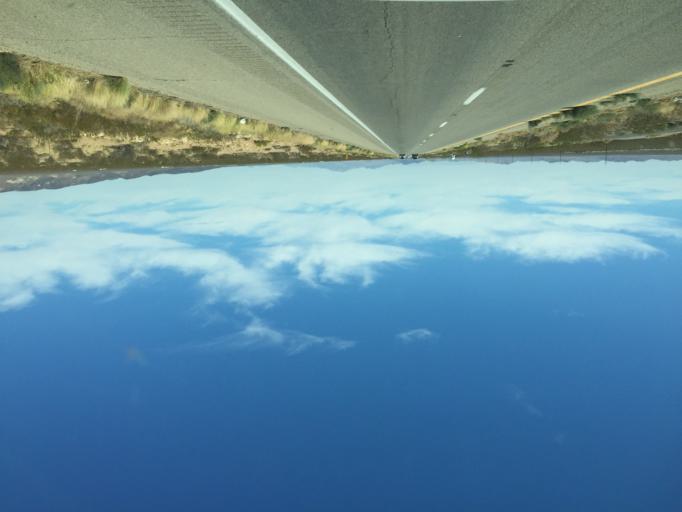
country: US
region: Arizona
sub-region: Mohave County
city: Dolan Springs
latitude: 35.5739
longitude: -114.3829
